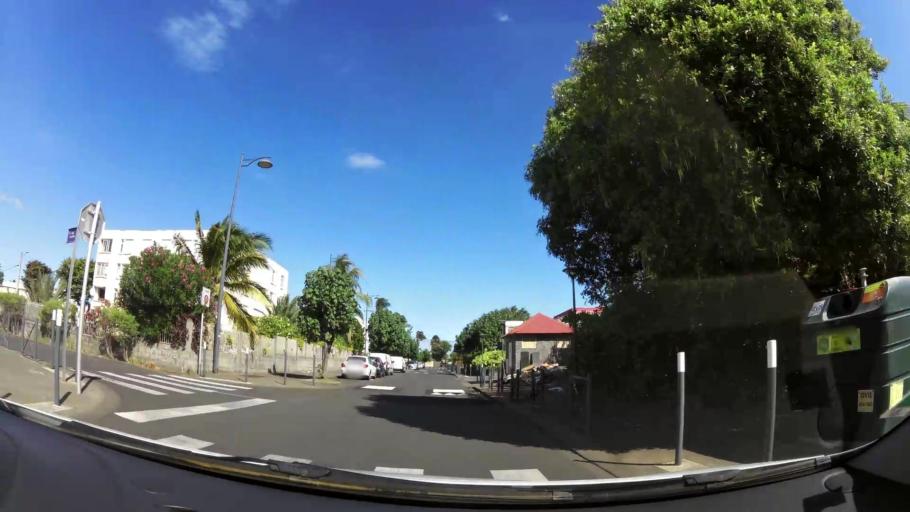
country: RE
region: Reunion
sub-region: Reunion
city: Saint-Pierre
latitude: -21.3400
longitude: 55.4632
